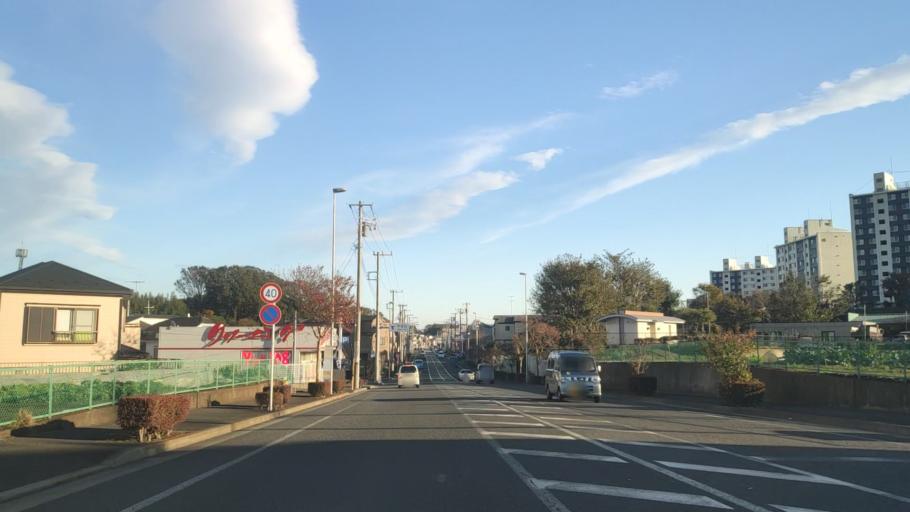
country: JP
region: Kanagawa
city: Fujisawa
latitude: 35.3923
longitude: 139.4923
